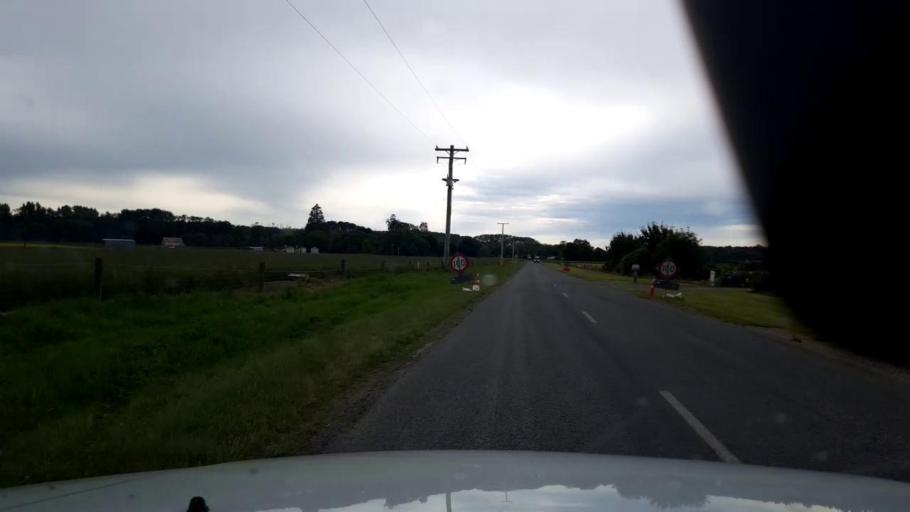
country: NZ
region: Canterbury
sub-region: Timaru District
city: Pleasant Point
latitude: -44.2700
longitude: 171.2586
